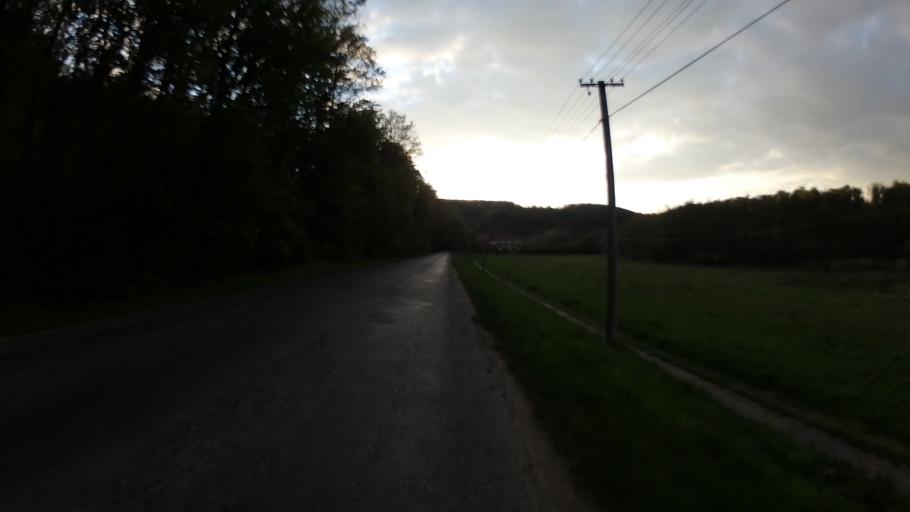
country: CZ
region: South Moravian
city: Strelice
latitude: 49.1371
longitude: 16.4721
